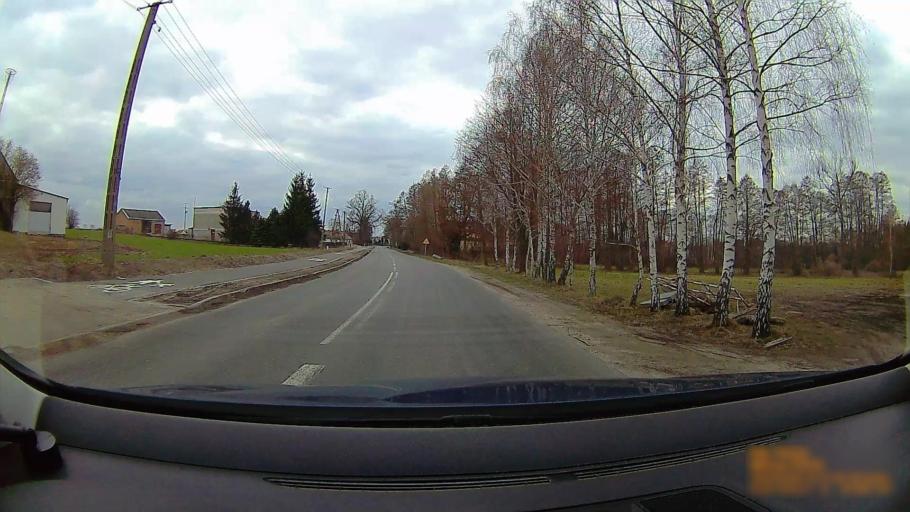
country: PL
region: Greater Poland Voivodeship
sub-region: Powiat koninski
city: Rzgow Pierwszy
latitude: 52.1810
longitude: 18.1018
